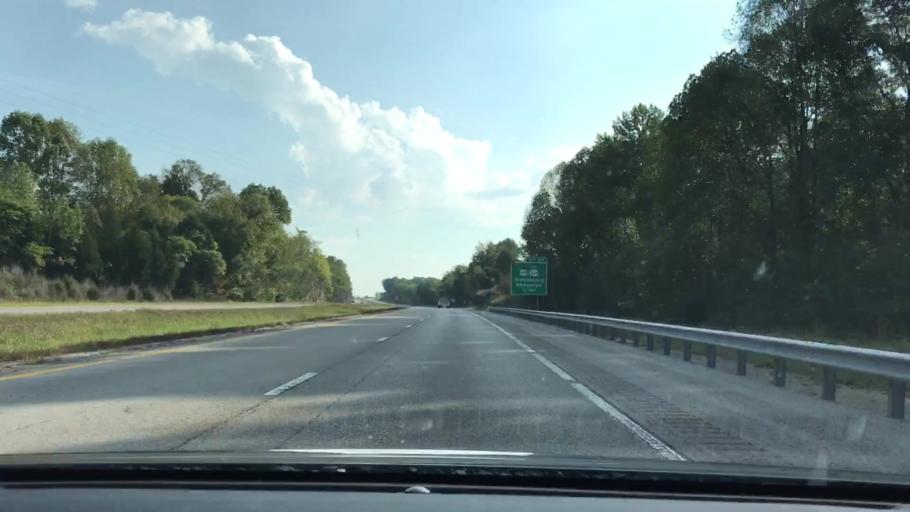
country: US
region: Kentucky
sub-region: Metcalfe County
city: Edmonton
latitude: 36.9972
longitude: -85.6316
